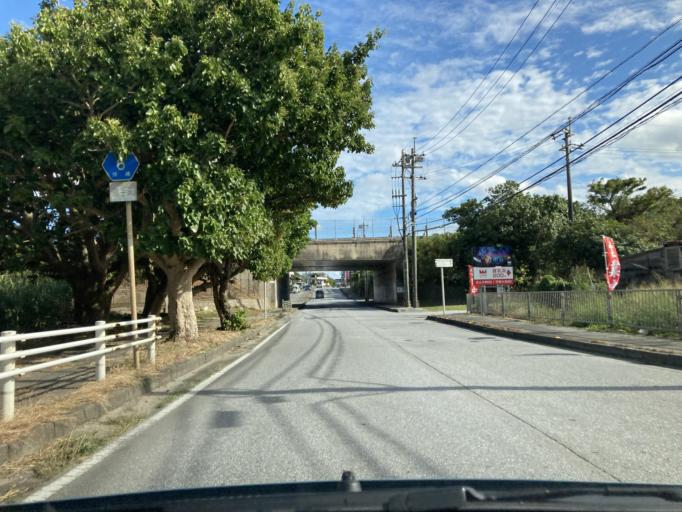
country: JP
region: Okinawa
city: Ishikawa
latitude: 26.4222
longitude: 127.8108
